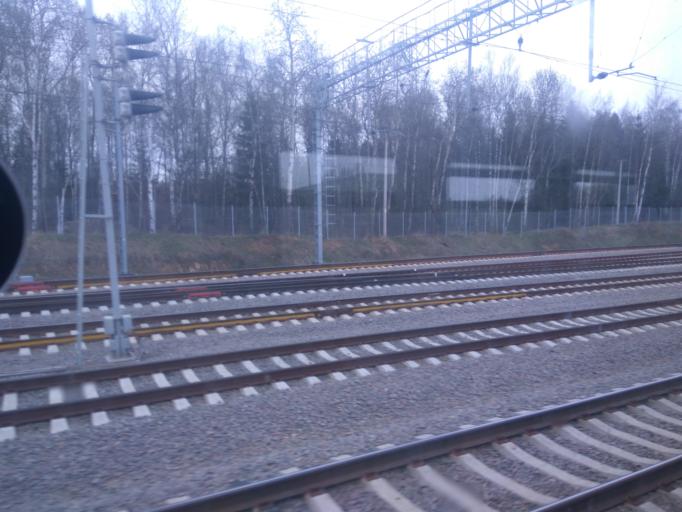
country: RU
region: Moskovskaya
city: Skoropuskovskiy
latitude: 56.3568
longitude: 38.1665
